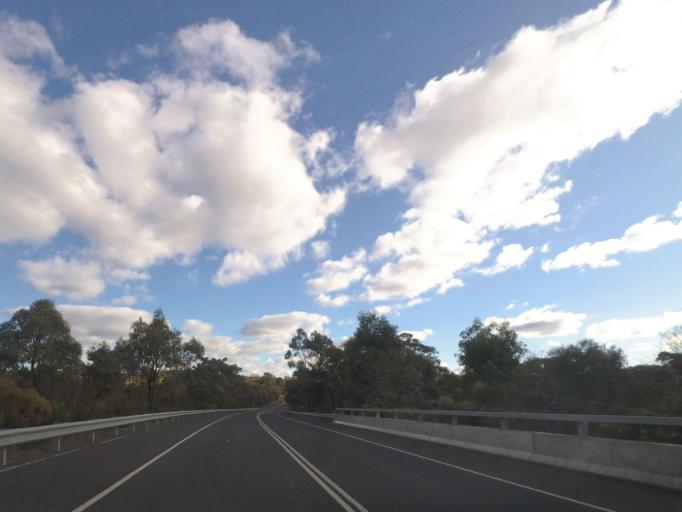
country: AU
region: Victoria
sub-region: Mount Alexander
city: Castlemaine
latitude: -37.1024
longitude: 144.3187
